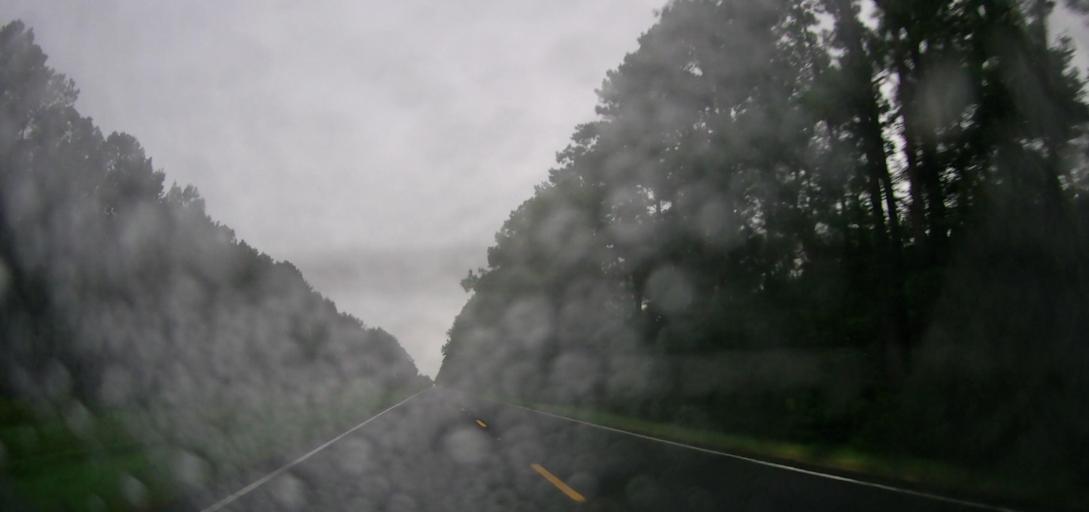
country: US
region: Georgia
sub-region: Glynn County
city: Dock Junction
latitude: 31.2645
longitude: -81.6309
